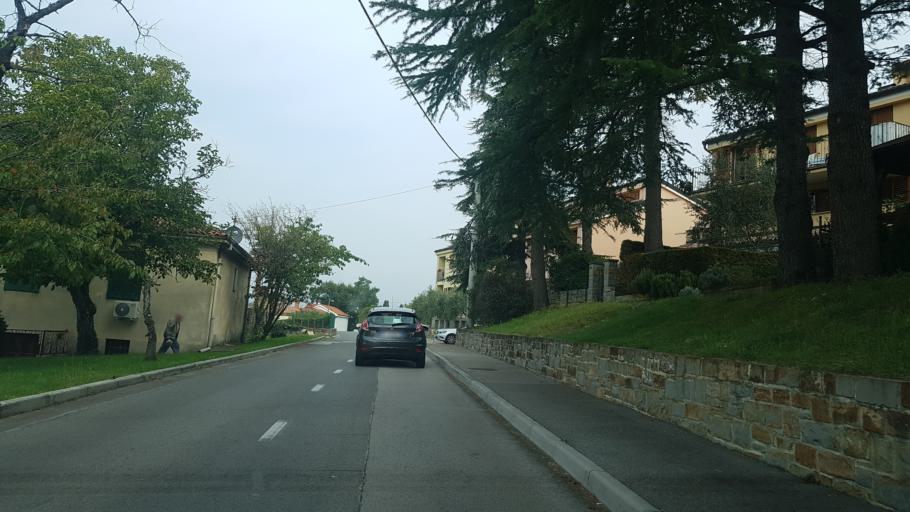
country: SI
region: Koper-Capodistria
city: Spodnje Skofije
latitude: 45.5740
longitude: 13.8029
